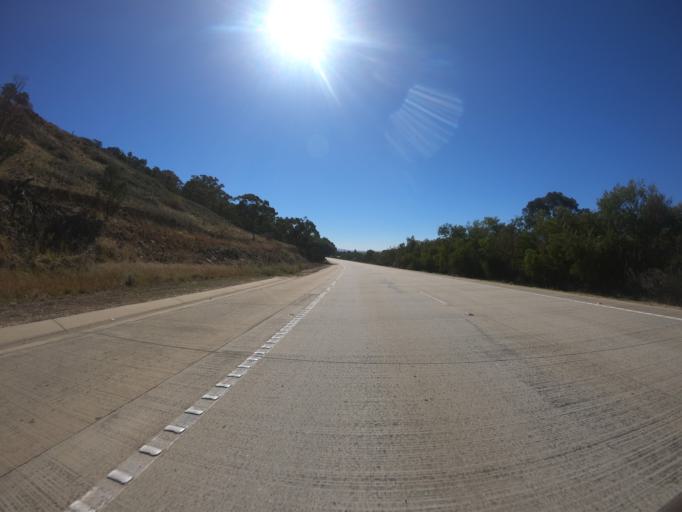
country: AU
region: New South Wales
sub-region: Yass Valley
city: Gundaroo
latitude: -35.0968
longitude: 149.3759
